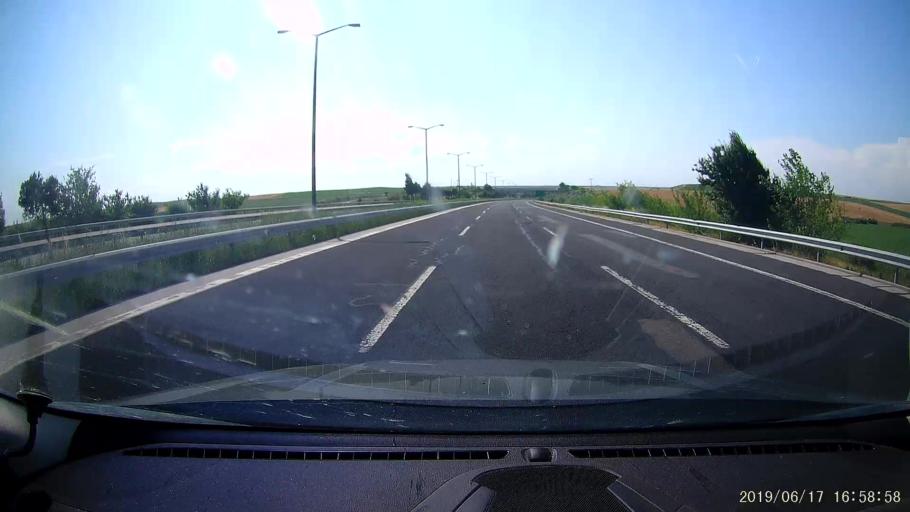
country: TR
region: Edirne
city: Haskoy
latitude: 41.6117
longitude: 26.8724
